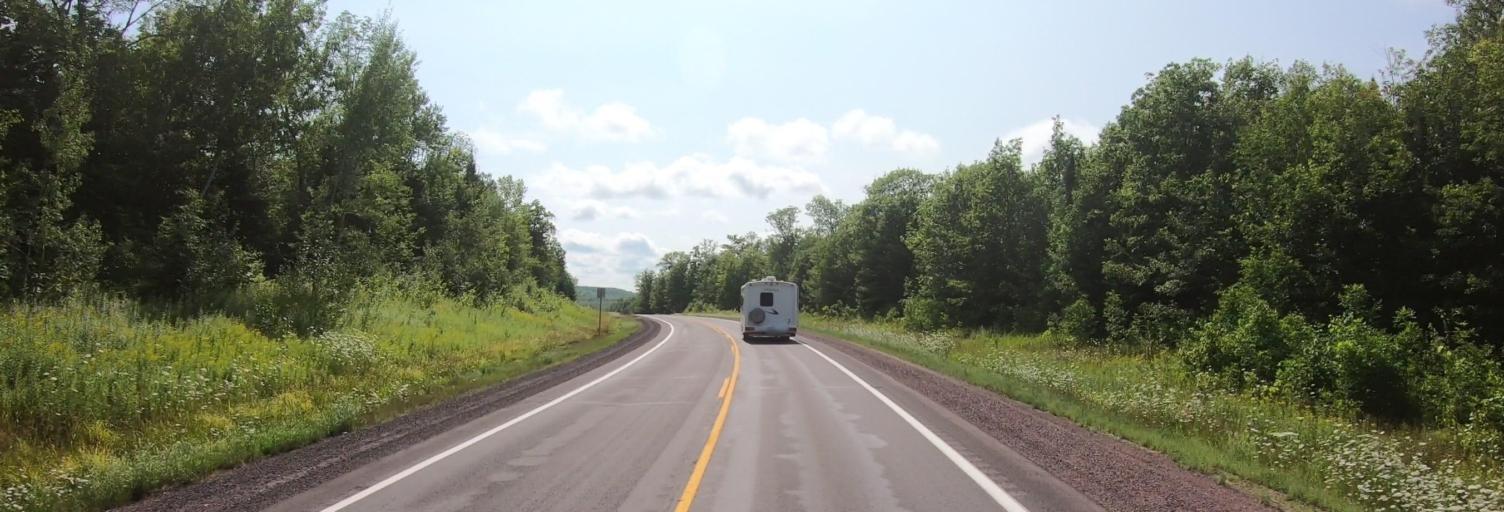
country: US
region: Michigan
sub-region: Ontonagon County
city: Ontonagon
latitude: 46.8593
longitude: -88.9526
